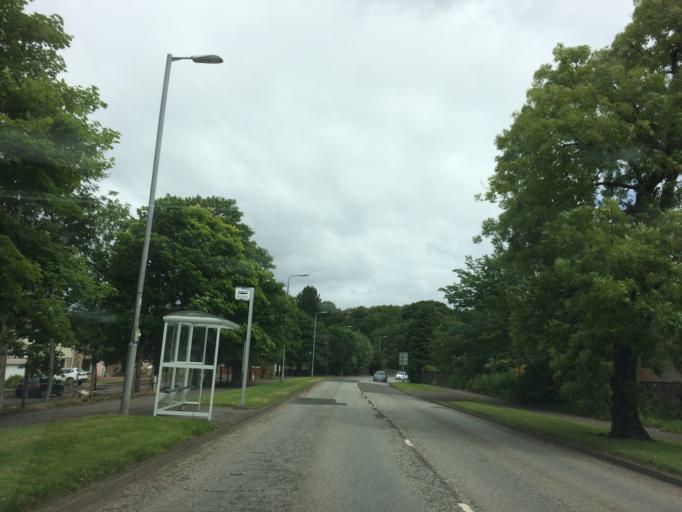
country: GB
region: Scotland
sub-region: East Renfrewshire
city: Newton Mearns
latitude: 55.7773
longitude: -4.3319
